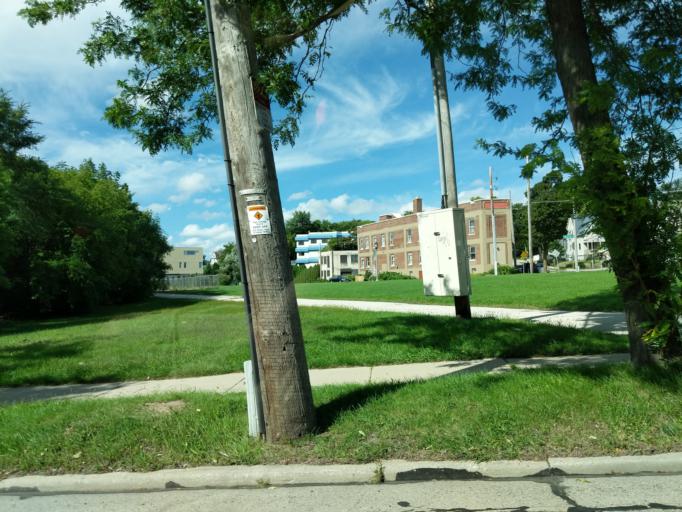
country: US
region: Wisconsin
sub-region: Milwaukee County
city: Milwaukee
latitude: 43.0588
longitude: -87.8980
